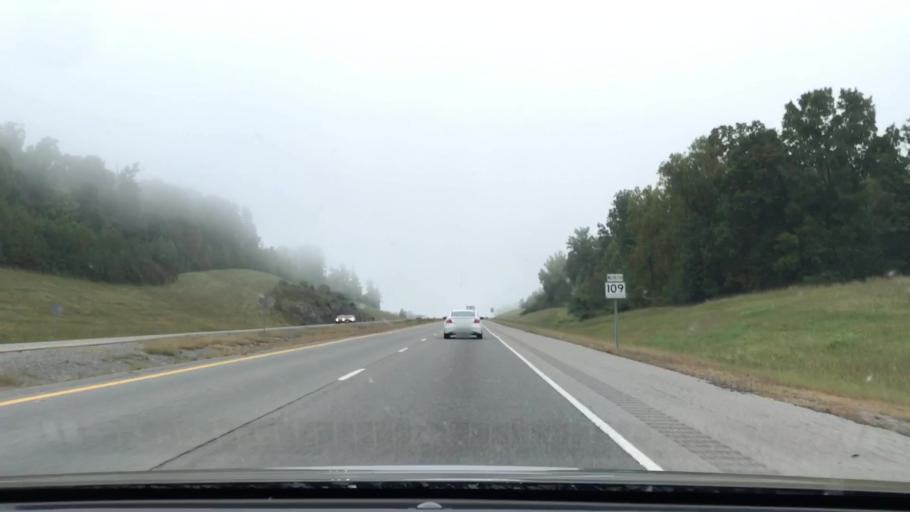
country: US
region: Tennessee
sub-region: Sumner County
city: Gallatin
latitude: 36.4721
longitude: -86.4733
